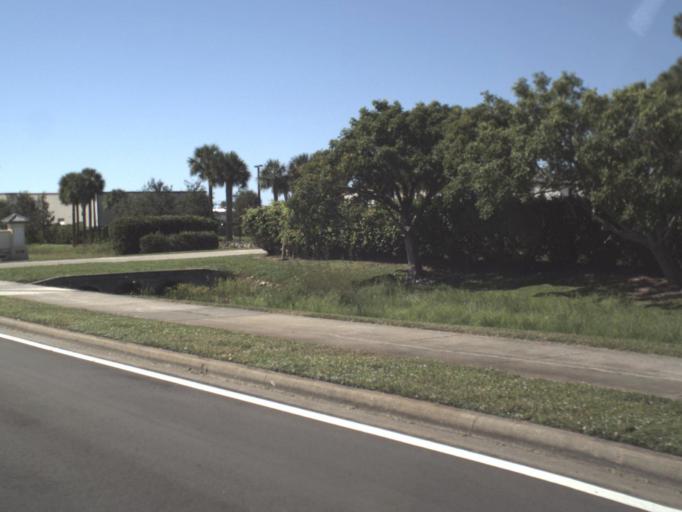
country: US
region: Florida
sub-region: Collier County
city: Naples
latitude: 26.1573
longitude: -81.7670
